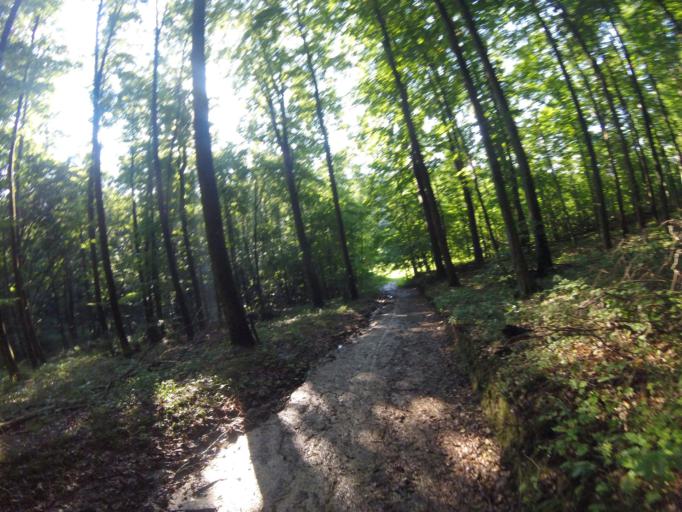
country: HU
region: Zala
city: Letenye
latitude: 46.5072
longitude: 16.7178
